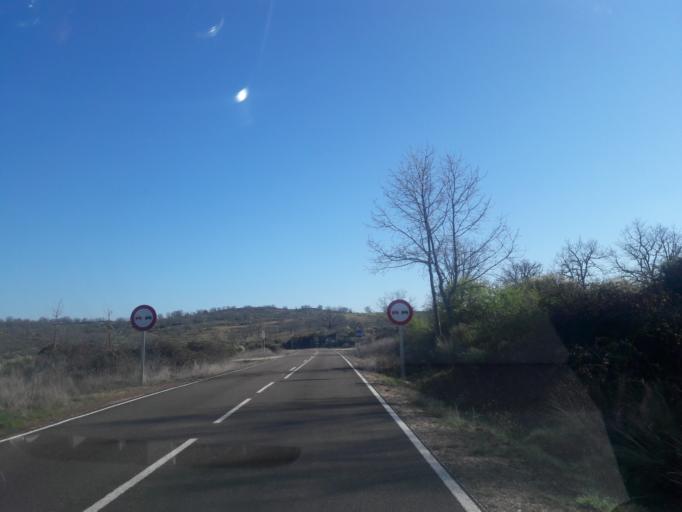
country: ES
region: Castille and Leon
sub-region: Provincia de Salamanca
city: Cabeza del Caballo
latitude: 41.0955
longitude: -6.5537
